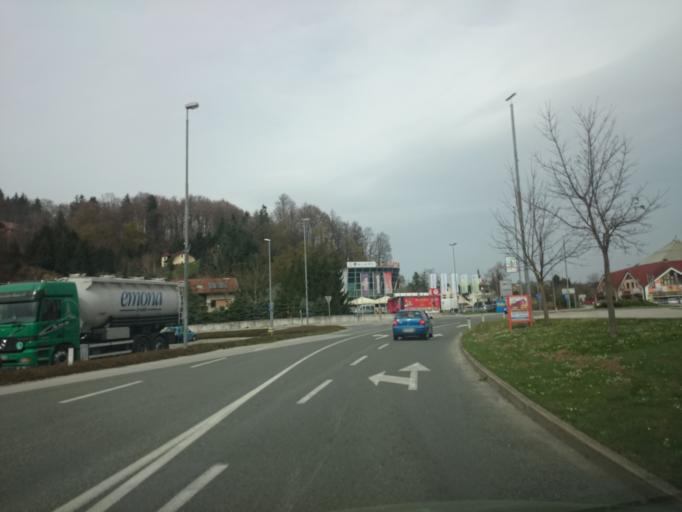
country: SI
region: Sentjur pri Celju
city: Sentjur
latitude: 46.2139
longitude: 15.3910
